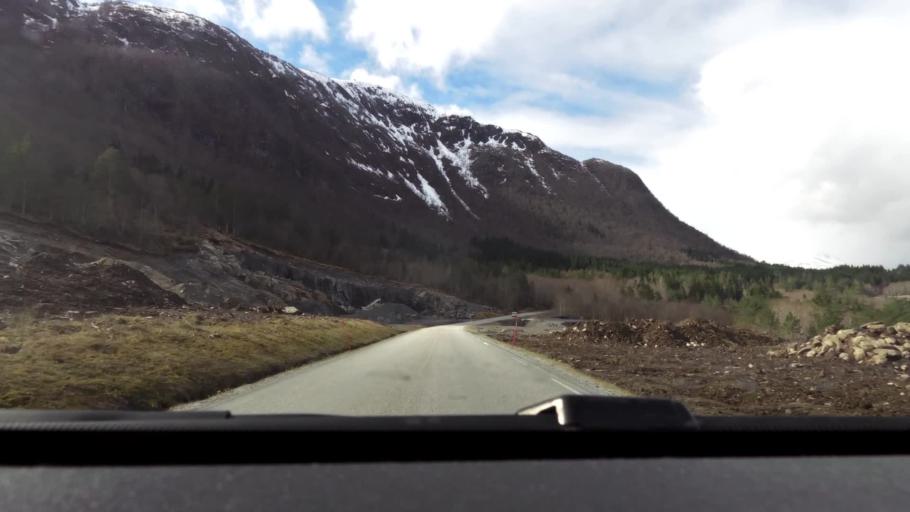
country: NO
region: More og Romsdal
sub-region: Averoy
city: Bruhagen
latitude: 63.0984
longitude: 7.6279
